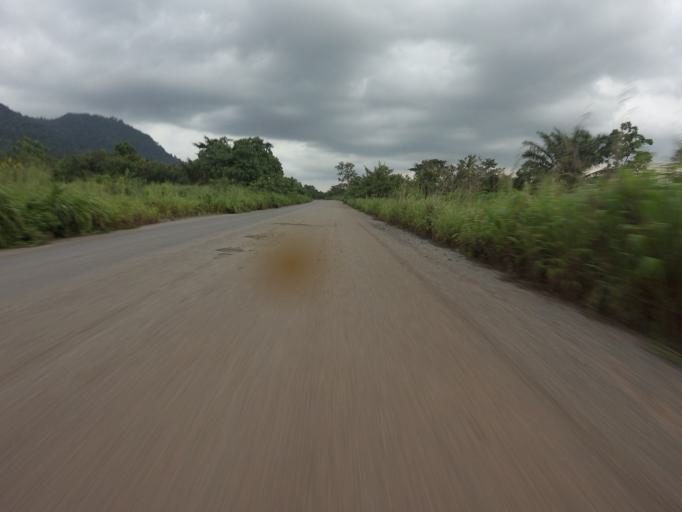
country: GH
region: Volta
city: Kpandu
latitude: 6.8054
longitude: 0.3737
